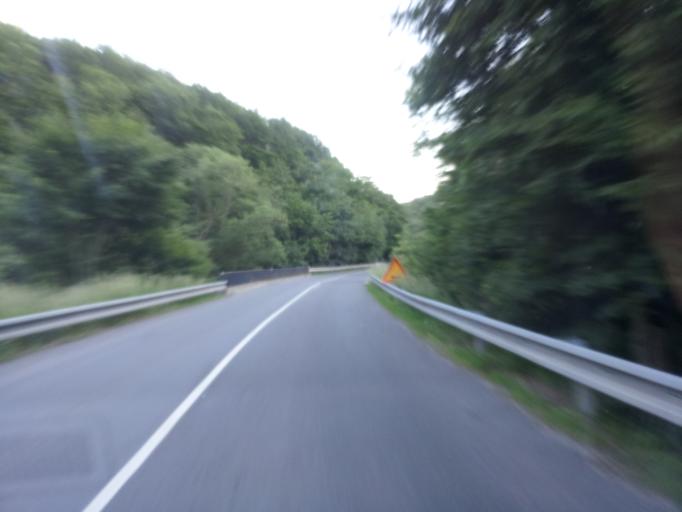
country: SK
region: Banskobystricky
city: Krupina
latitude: 48.3270
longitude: 18.9779
